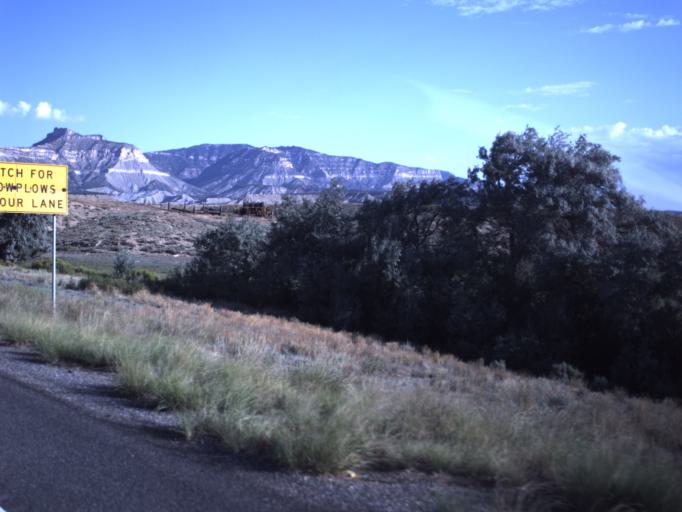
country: US
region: Utah
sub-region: Emery County
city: Huntington
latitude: 39.3402
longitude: -110.9777
